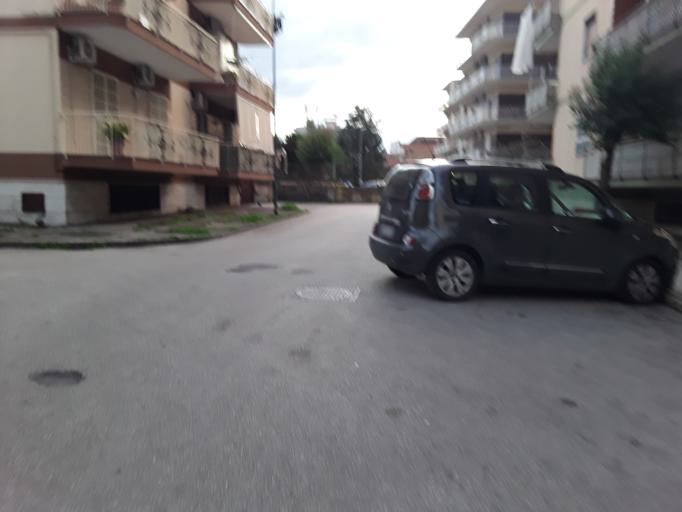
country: IT
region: Campania
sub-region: Provincia di Napoli
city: Volla
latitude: 40.8751
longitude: 14.3394
